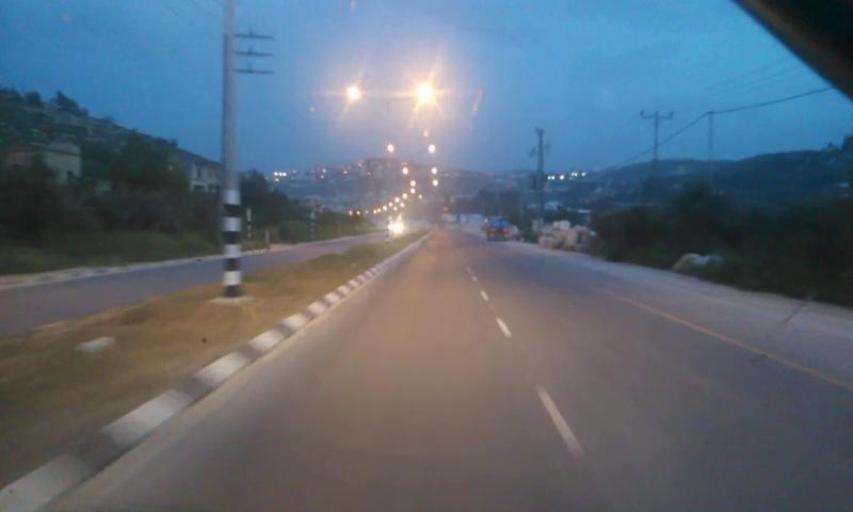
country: PS
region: West Bank
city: Dayr Sharaf
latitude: 32.2464
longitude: 35.1931
